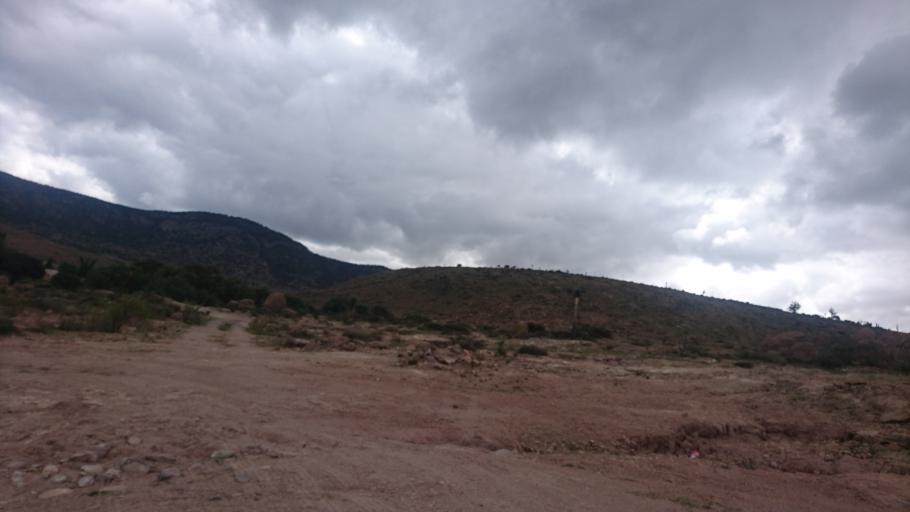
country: MX
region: San Luis Potosi
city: Escalerillas
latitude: 22.0748
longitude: -101.0978
